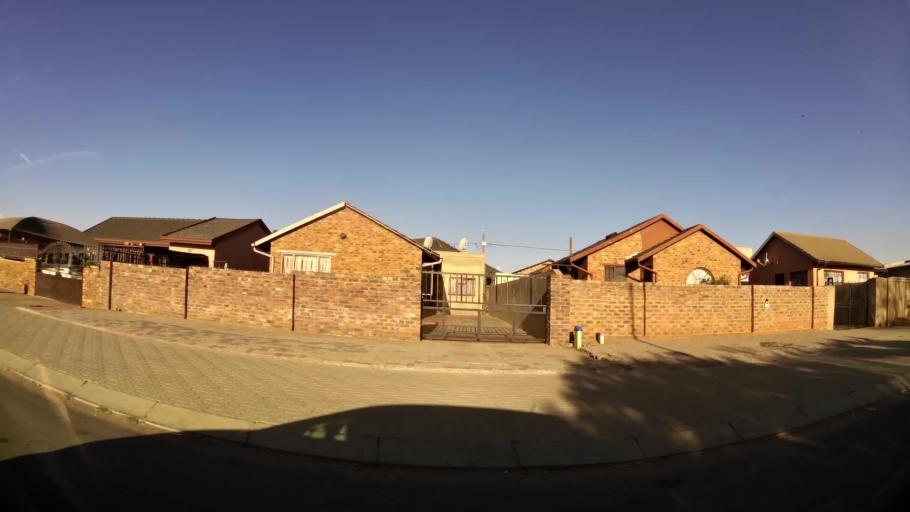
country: ZA
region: Gauteng
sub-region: Ekurhuleni Metropolitan Municipality
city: Tembisa
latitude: -26.0129
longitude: 28.2276
